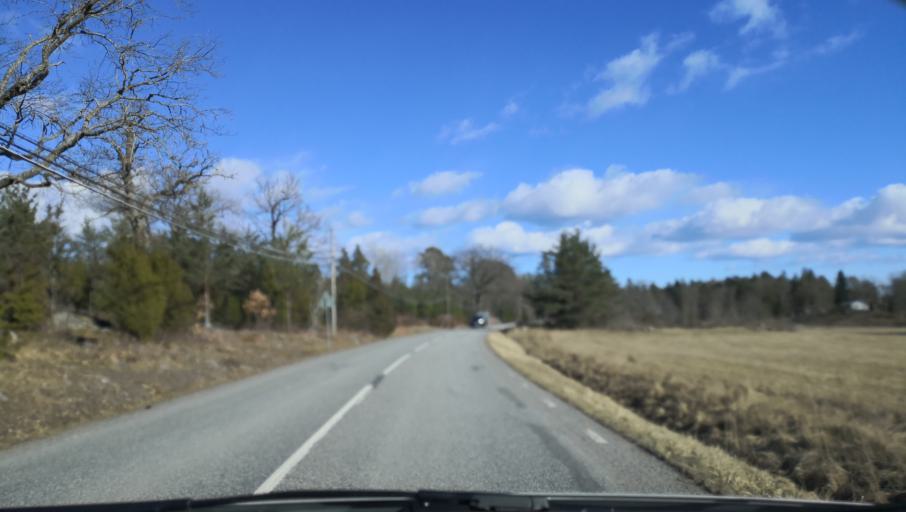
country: SE
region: Stockholm
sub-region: Varmdo Kommun
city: Holo
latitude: 59.3559
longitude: 18.6090
